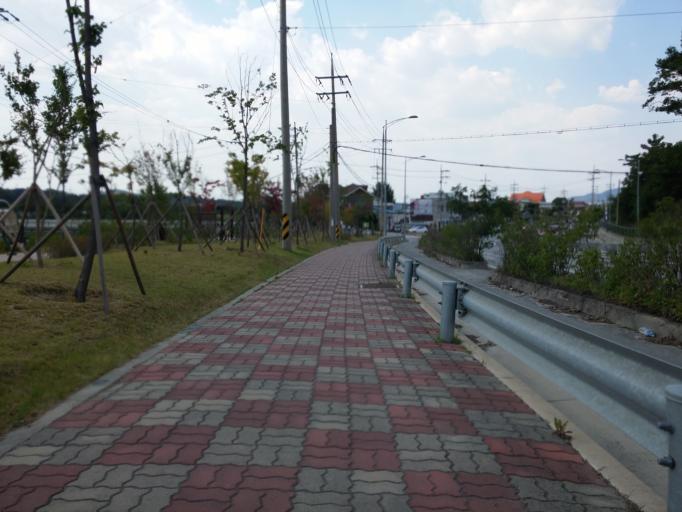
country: KR
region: Chungcheongbuk-do
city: Cheongju-si
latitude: 36.5639
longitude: 127.5099
